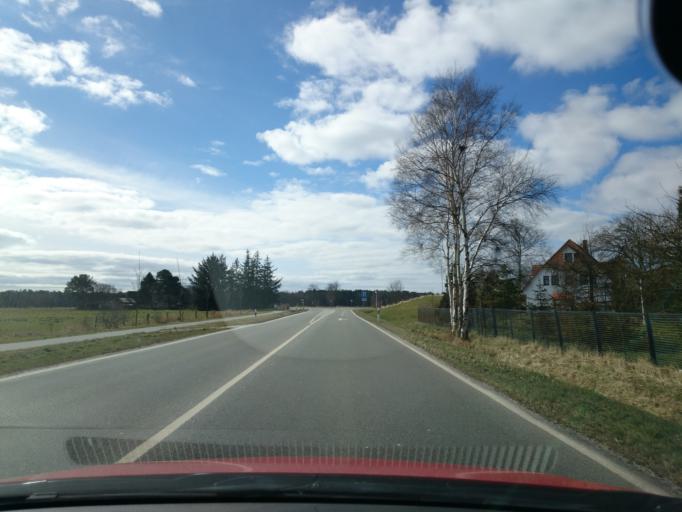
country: DE
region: Mecklenburg-Vorpommern
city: Ostseebad Prerow
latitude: 54.4411
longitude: 12.5814
